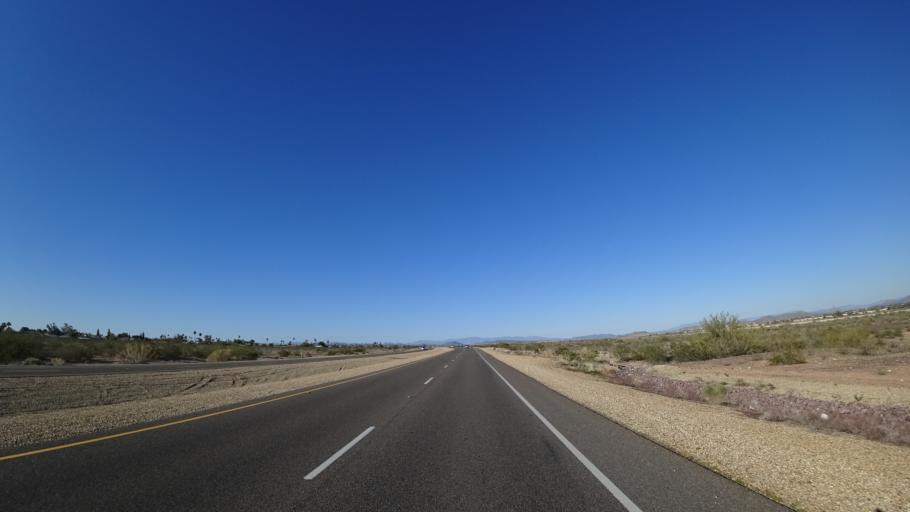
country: US
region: Arizona
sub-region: Maricopa County
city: Surprise
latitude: 33.6492
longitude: -112.3226
